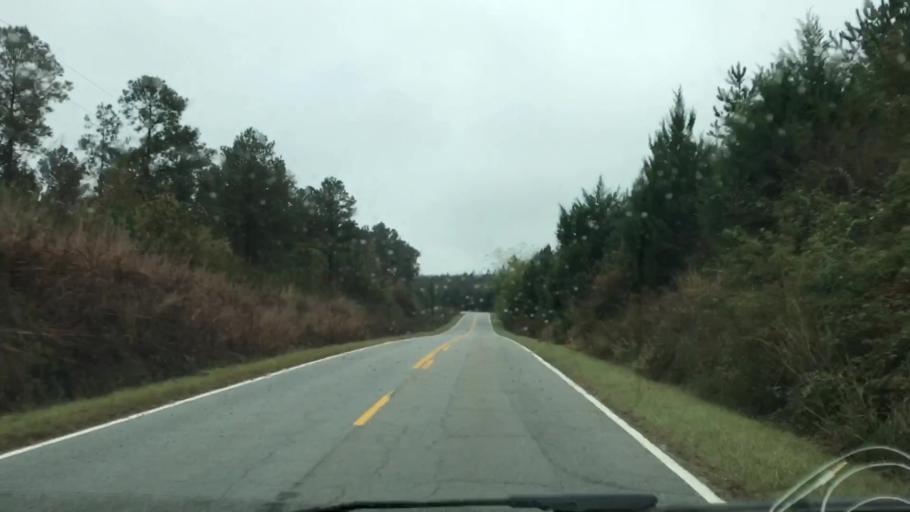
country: US
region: South Carolina
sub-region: Laurens County
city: Joanna
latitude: 34.3754
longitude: -81.7800
